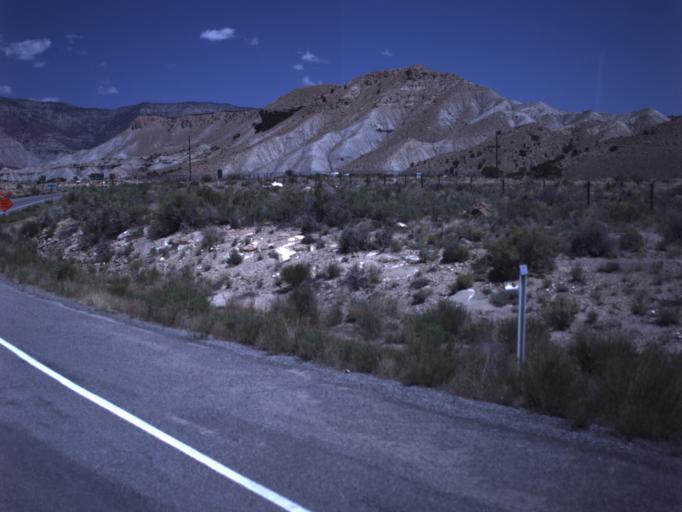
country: US
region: Utah
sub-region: Emery County
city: Orangeville
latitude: 39.2525
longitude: -111.0974
